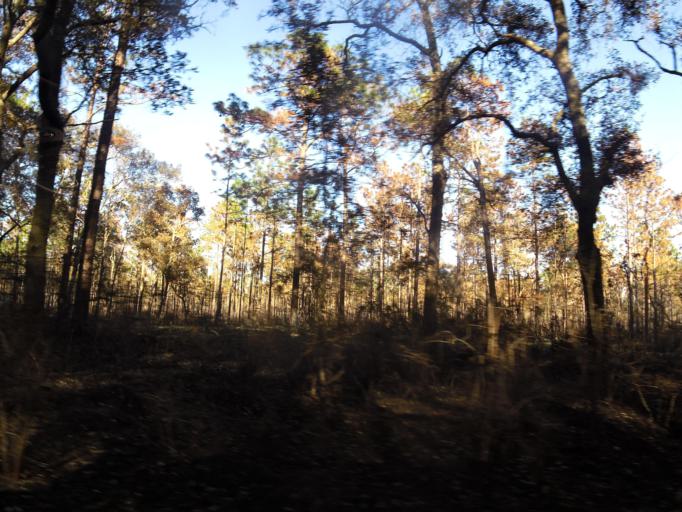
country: US
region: Florida
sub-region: Clay County
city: Middleburg
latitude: 30.1401
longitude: -81.9058
